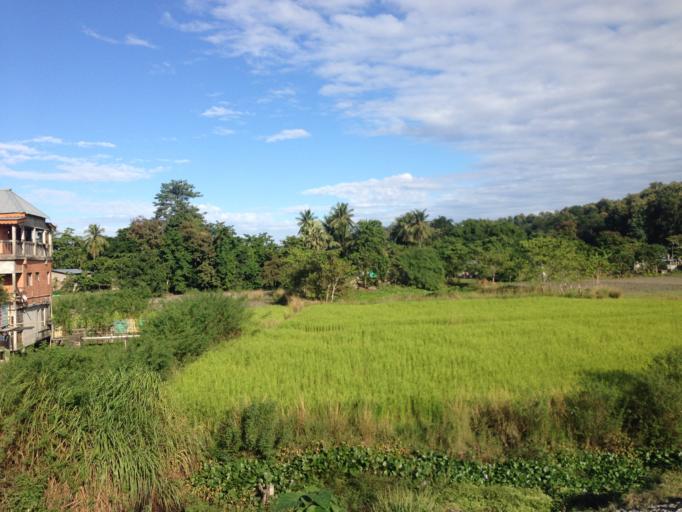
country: IN
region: Assam
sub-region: Sontipur
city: Tezpur
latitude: 26.6198
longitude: 92.8506
